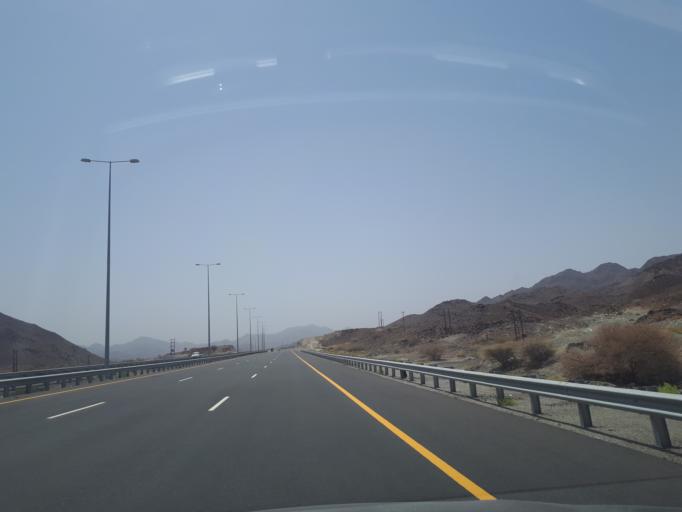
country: OM
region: Ash Sharqiyah
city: Ibra'
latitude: 22.8635
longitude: 58.3075
